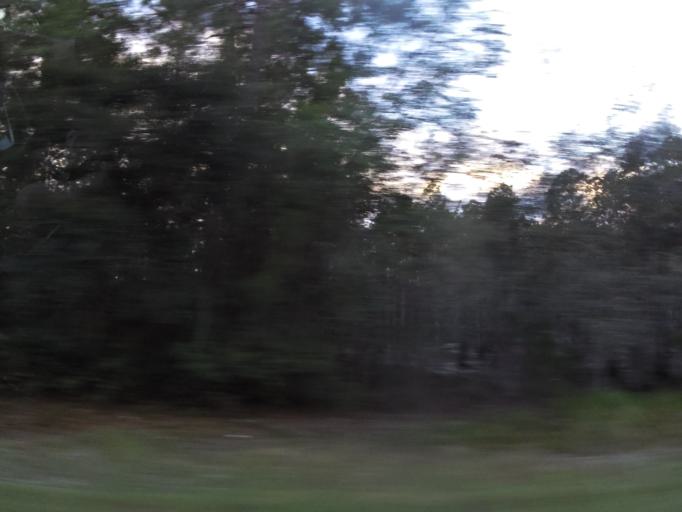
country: US
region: Georgia
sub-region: Echols County
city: Statenville
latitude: 30.7405
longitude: -83.0973
